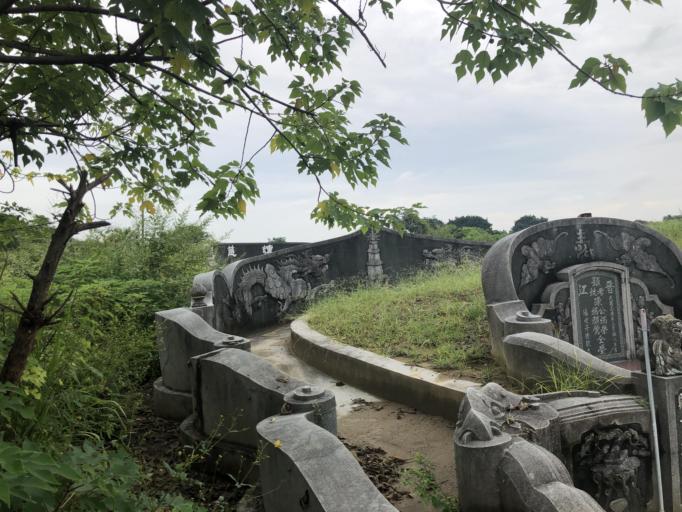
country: TW
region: Taiwan
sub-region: Tainan
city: Tainan
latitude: 22.9650
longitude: 120.1983
